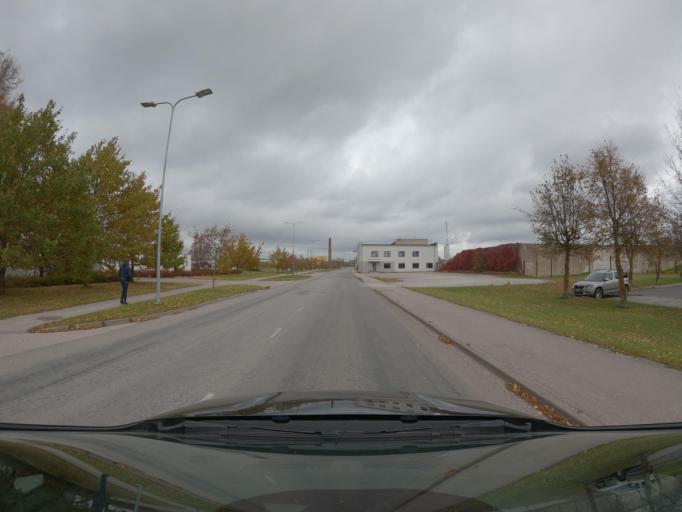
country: EE
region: Saare
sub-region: Kuressaare linn
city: Kuressaare
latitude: 58.2651
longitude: 22.4872
